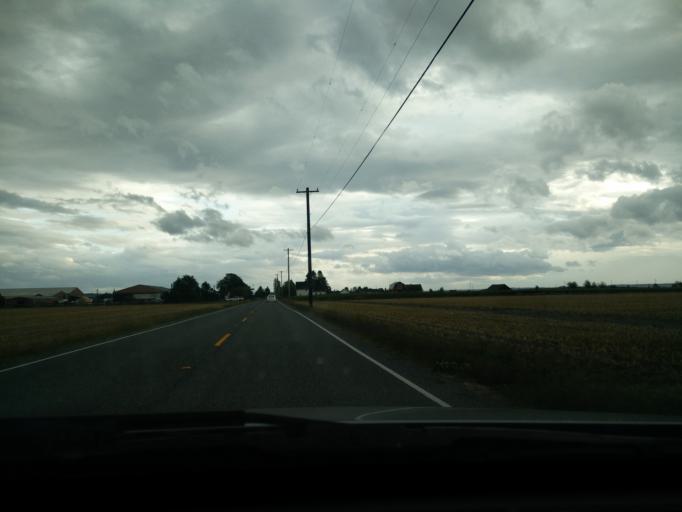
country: US
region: Washington
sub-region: Snohomish County
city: Stanwood
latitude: 48.2540
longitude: -122.3709
